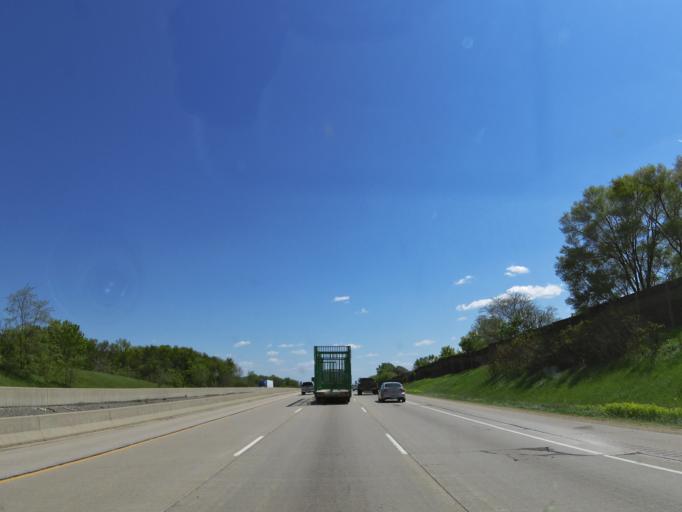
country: US
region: Wisconsin
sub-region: Dane County
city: Monona
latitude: 43.0830
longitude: -89.2833
